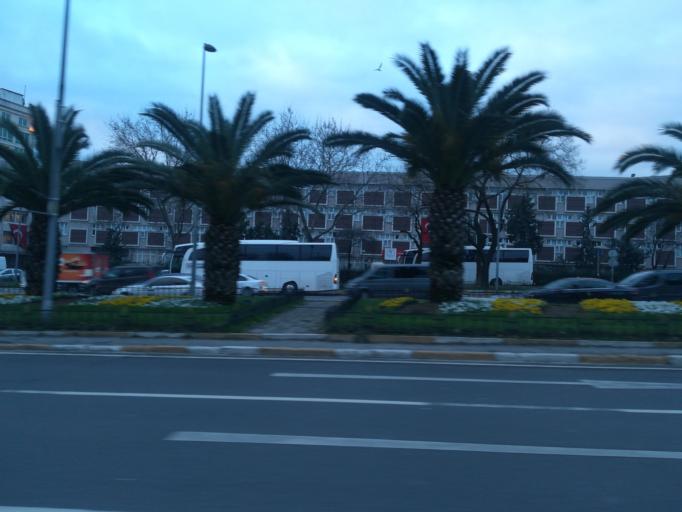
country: TR
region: Istanbul
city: Istanbul
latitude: 41.0240
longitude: 28.9302
